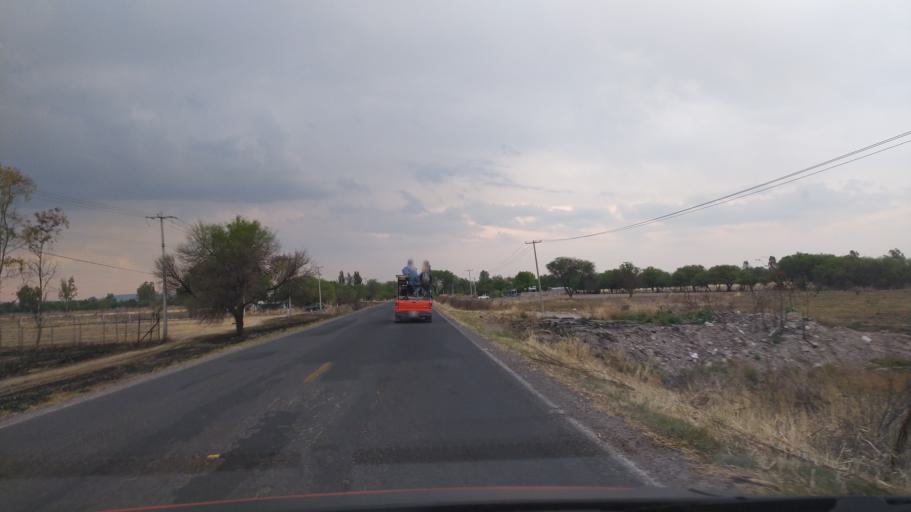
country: MX
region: Guanajuato
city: Ciudad Manuel Doblado
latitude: 20.7853
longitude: -101.9082
